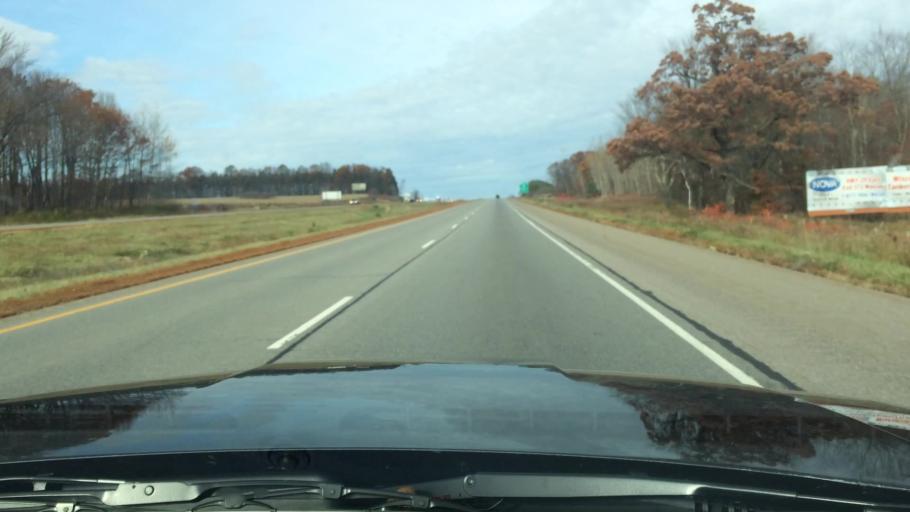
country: US
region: Wisconsin
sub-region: Marathon County
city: Mosinee
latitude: 44.7632
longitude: -89.6799
